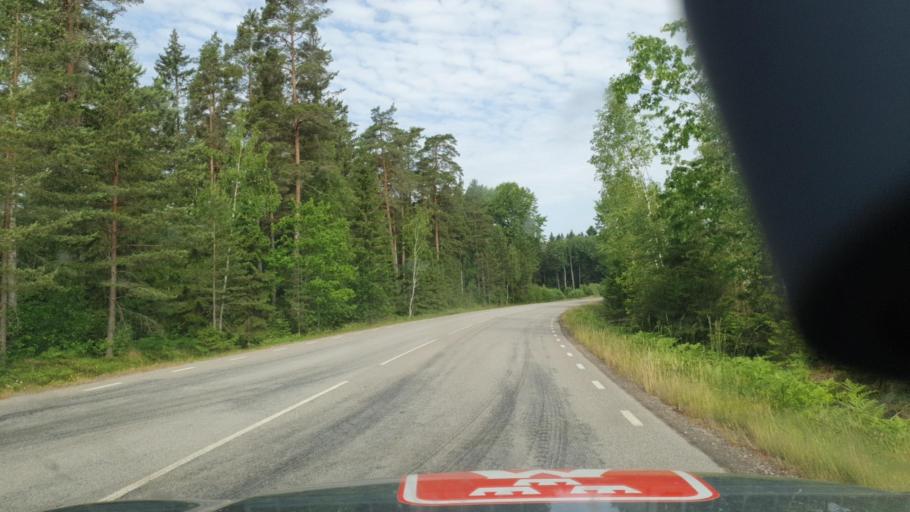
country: SE
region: Kalmar
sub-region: Nybro Kommun
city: Nybro
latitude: 56.7243
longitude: 15.9660
